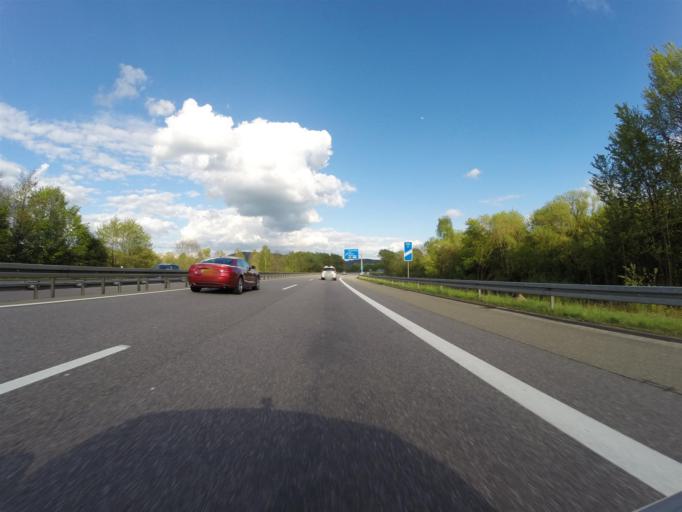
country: DE
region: Saarland
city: Mettlach
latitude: 49.4601
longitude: 6.5983
